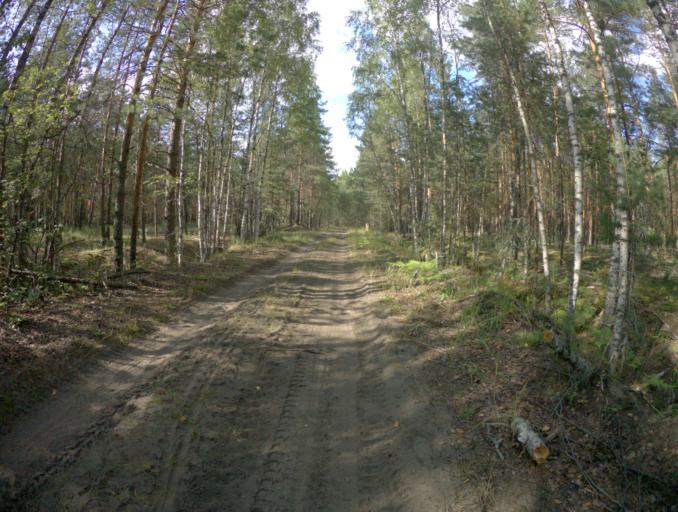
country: RU
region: Vladimir
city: Sobinka
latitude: 55.9493
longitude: 40.0590
